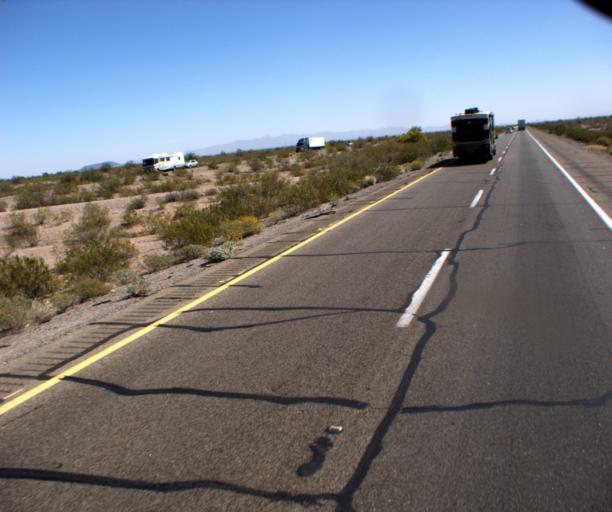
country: US
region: Arizona
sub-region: Maricopa County
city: Buckeye
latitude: 33.5066
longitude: -112.9888
